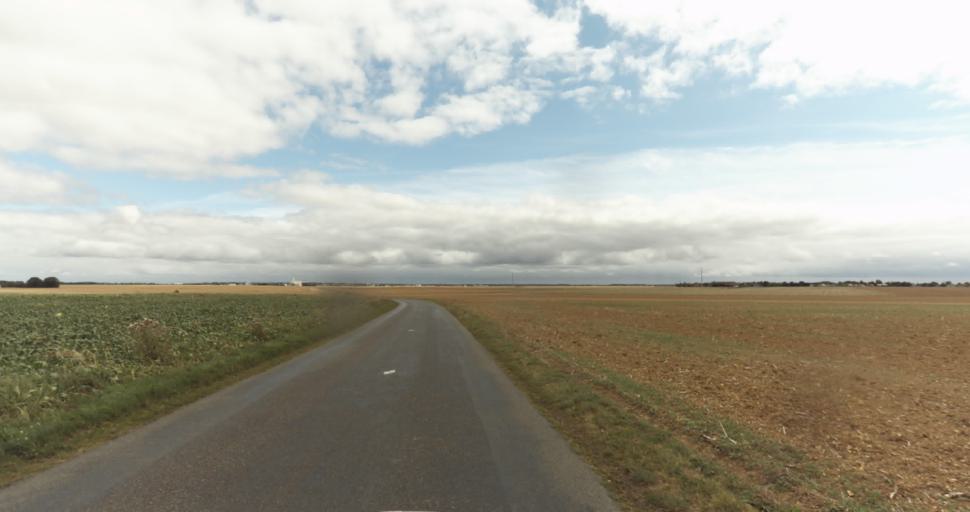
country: FR
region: Haute-Normandie
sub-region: Departement de l'Eure
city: Evreux
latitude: 48.9127
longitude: 1.2296
